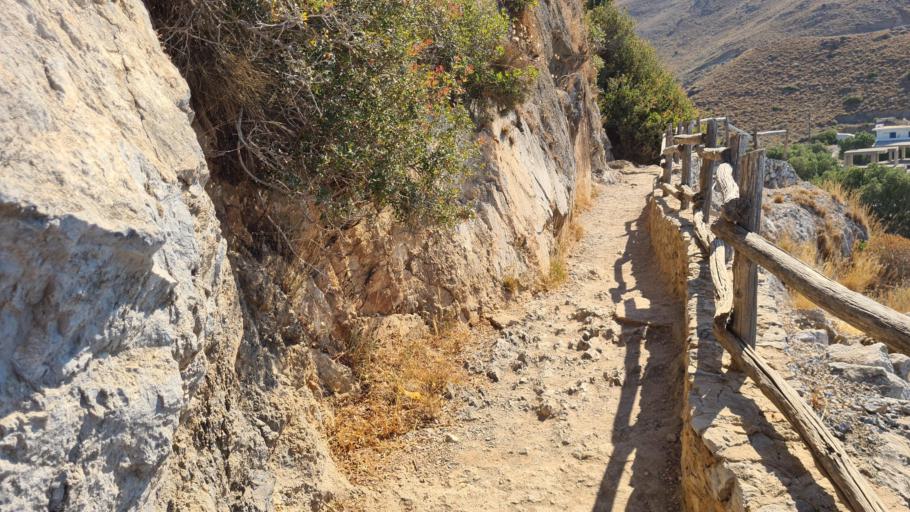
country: GR
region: Crete
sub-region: Nomos Rethymnis
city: Agia Foteini
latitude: 35.1534
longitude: 24.4768
